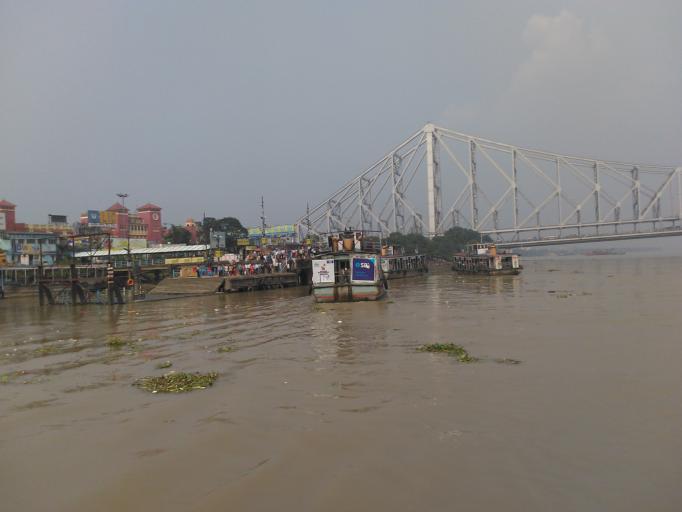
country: IN
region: West Bengal
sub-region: Kolkata
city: Bara Bazar
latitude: 22.5821
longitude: 88.3445
